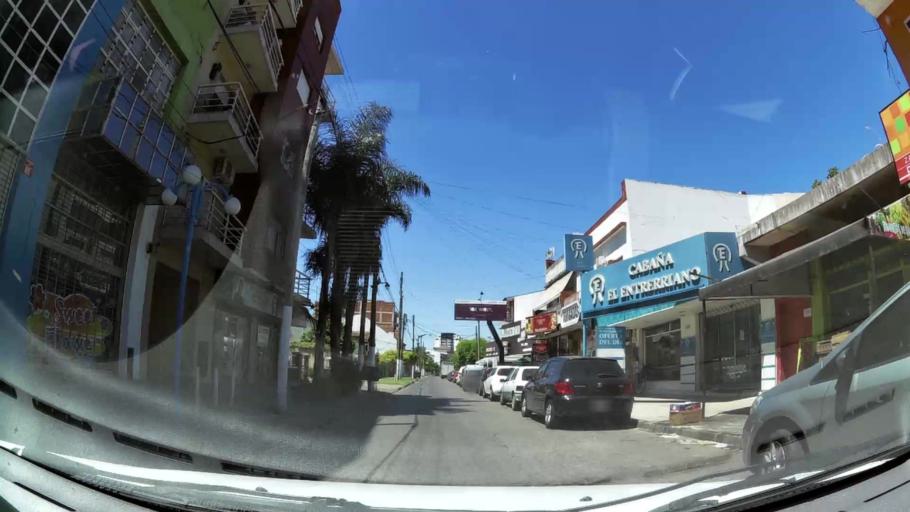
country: AR
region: Buenos Aires
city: Caseros
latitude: -34.5897
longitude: -58.5707
